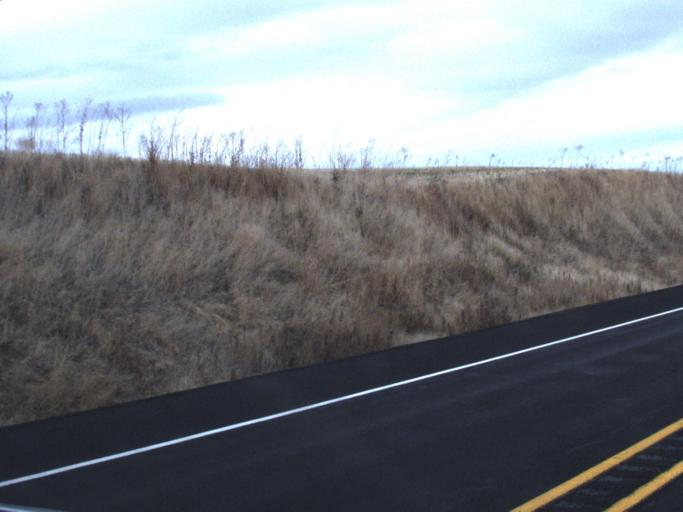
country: US
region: Washington
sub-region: Whitman County
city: Pullman
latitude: 46.5866
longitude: -117.1632
